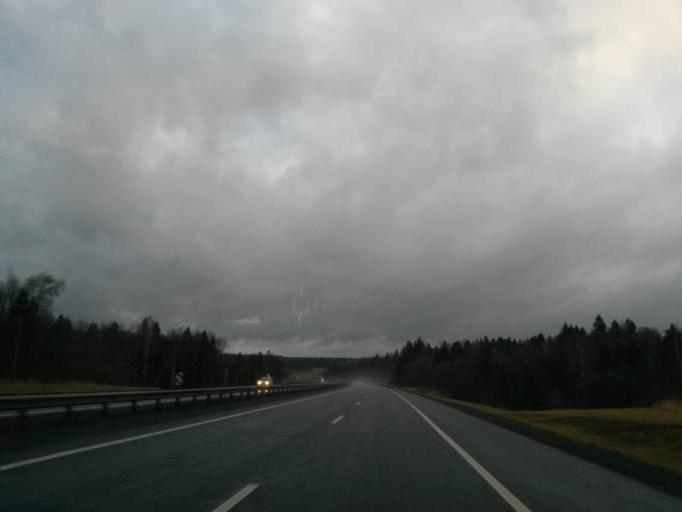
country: RU
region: Vladimir
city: Arsaki
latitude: 56.4729
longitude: 38.3909
